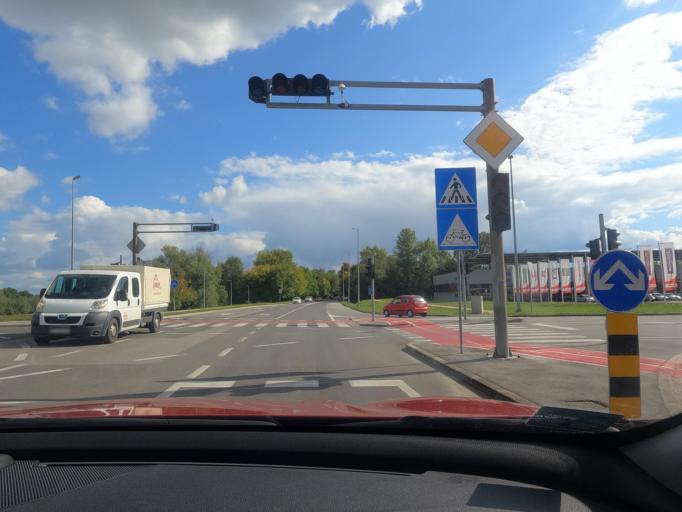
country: HR
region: Sisacko-Moslavacka
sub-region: Grad Sisak
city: Sisak
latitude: 45.4958
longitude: 16.3804
